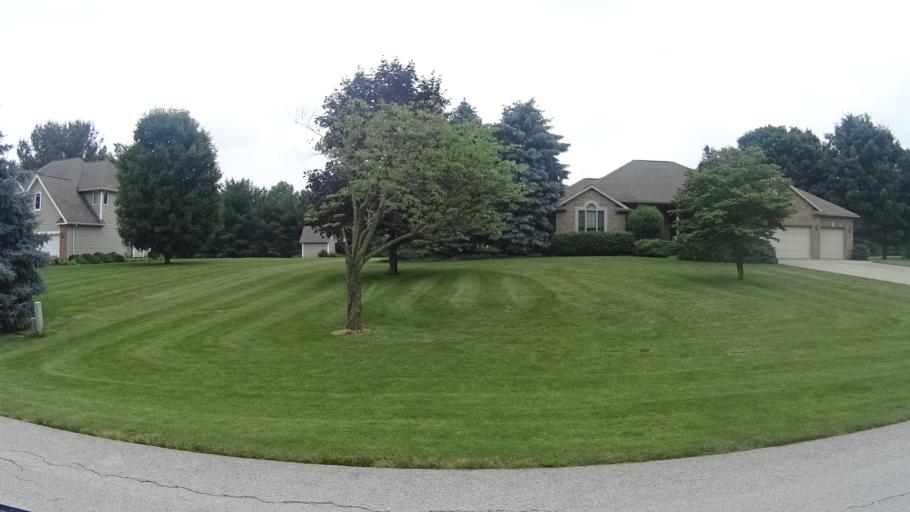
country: US
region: Ohio
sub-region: Erie County
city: Milan
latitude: 41.3013
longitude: -82.5839
